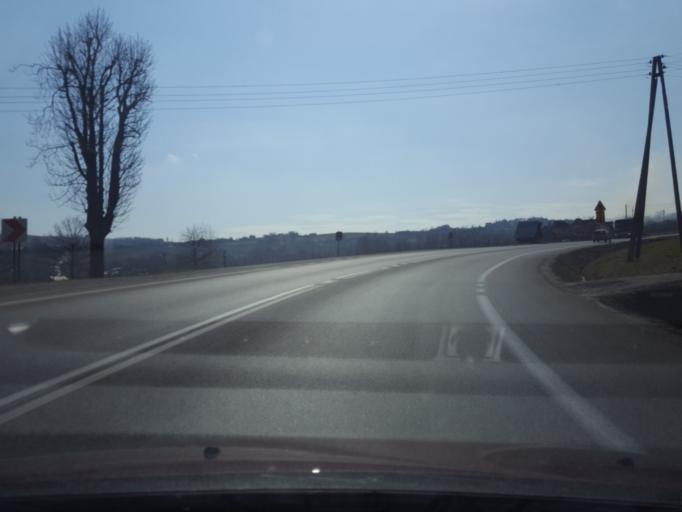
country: PL
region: Lesser Poland Voivodeship
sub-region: Powiat nowosadecki
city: Lososina Dolna
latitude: 49.7378
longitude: 20.6371
